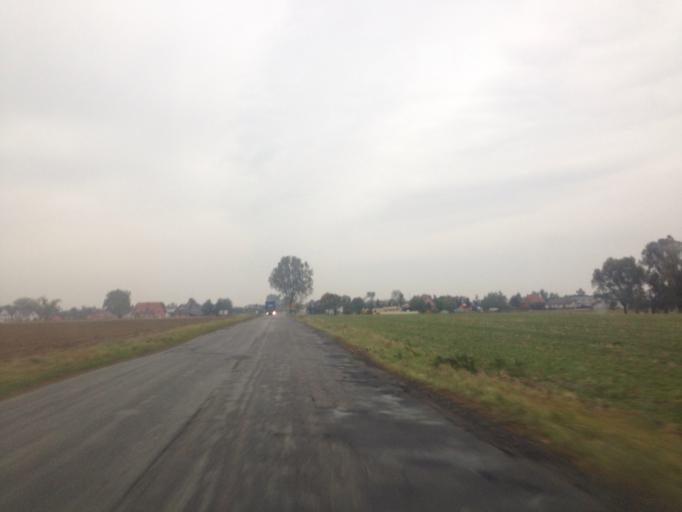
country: PL
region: Greater Poland Voivodeship
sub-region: Powiat poznanski
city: Kleszczewo
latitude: 52.3579
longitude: 17.1364
